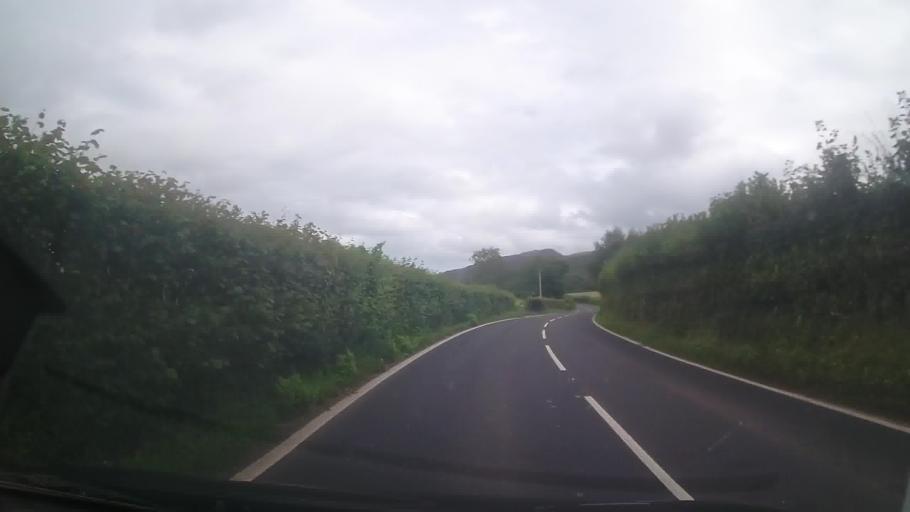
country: GB
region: Wales
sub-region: County of Ceredigion
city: Bow Street
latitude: 52.5286
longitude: -3.9573
